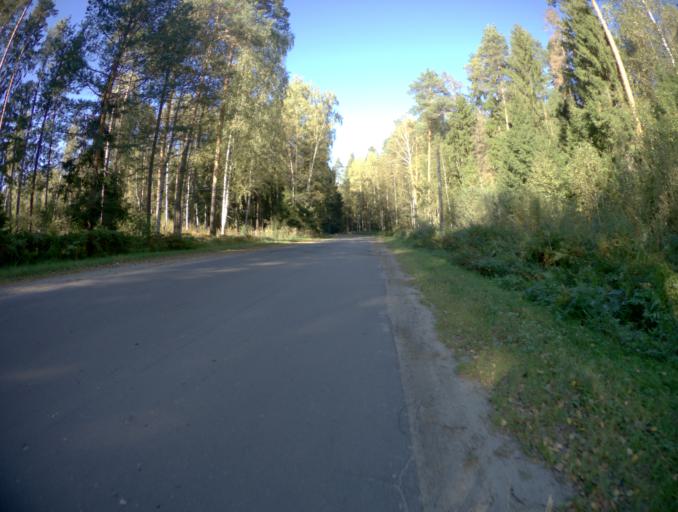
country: RU
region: Vladimir
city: Raduzhnyy
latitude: 55.9514
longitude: 40.2499
